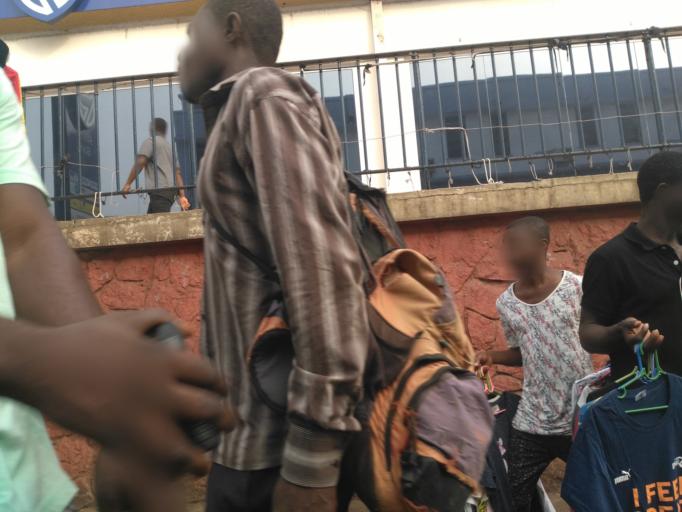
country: GH
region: Ashanti
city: Kumasi
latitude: 6.6950
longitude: -1.6217
